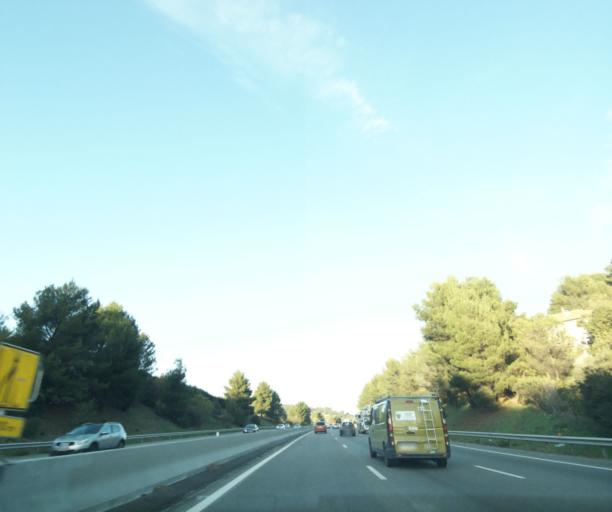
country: FR
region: Provence-Alpes-Cote d'Azur
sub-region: Departement des Bouches-du-Rhone
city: Roquevaire
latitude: 43.3413
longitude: 5.6101
